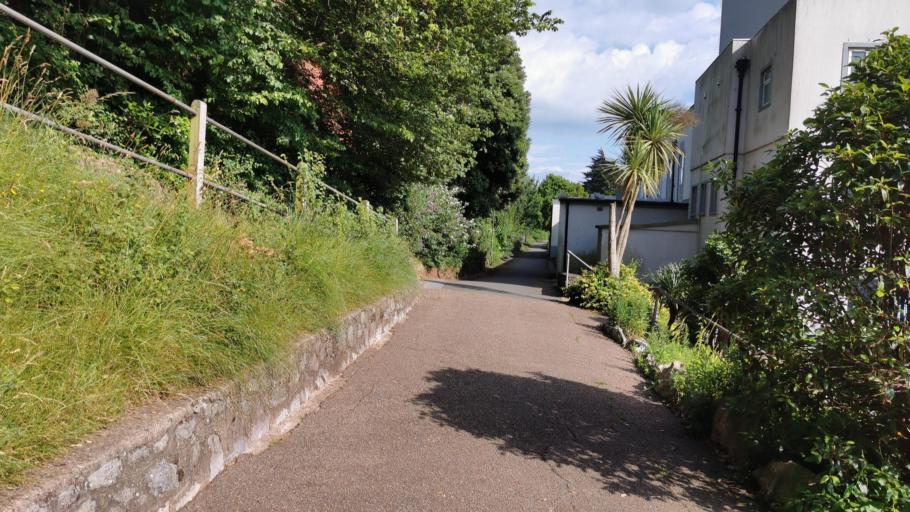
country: GB
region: England
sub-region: Devon
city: Exmouth
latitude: 50.6154
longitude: -3.4120
